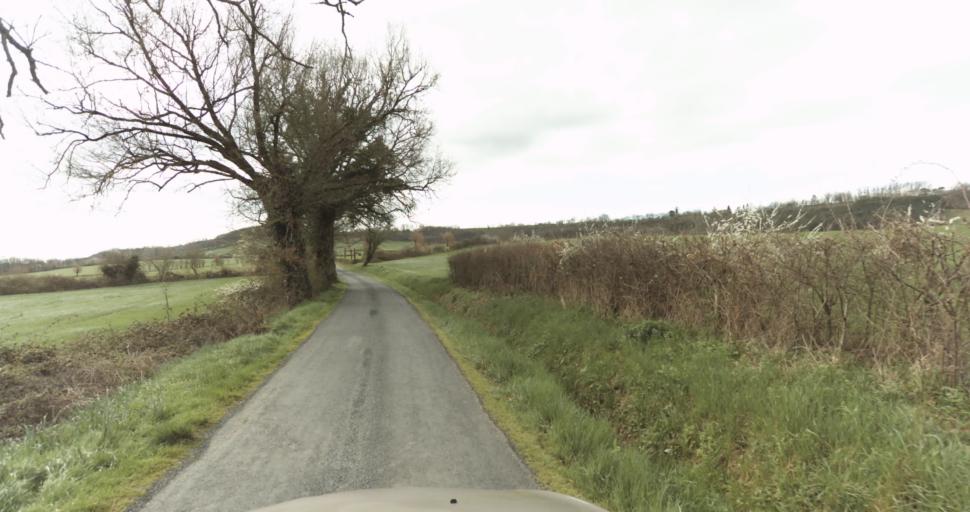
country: FR
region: Midi-Pyrenees
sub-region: Departement du Tarn
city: Frejairolles
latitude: 43.8756
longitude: 2.2033
